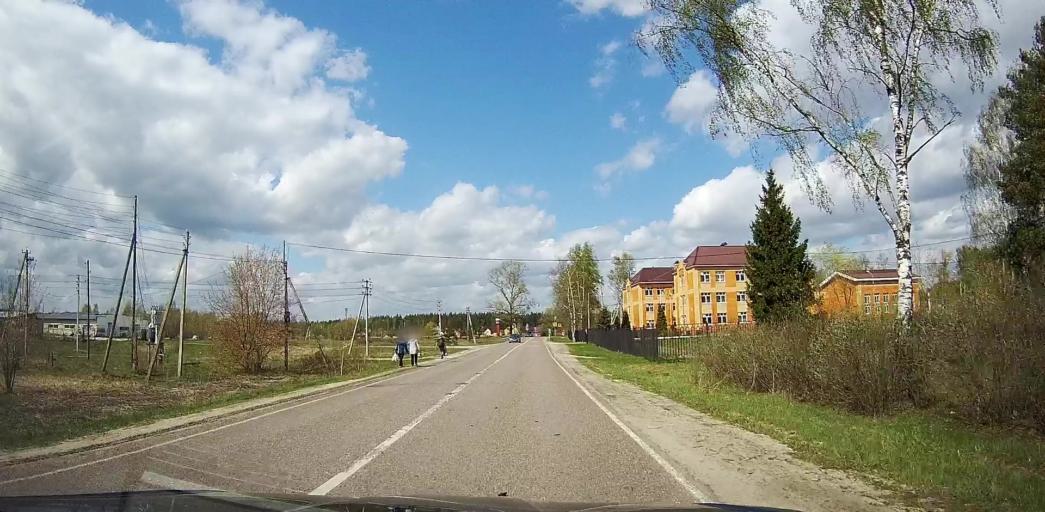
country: RU
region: Moskovskaya
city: Davydovo
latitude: 55.5575
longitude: 38.8139
